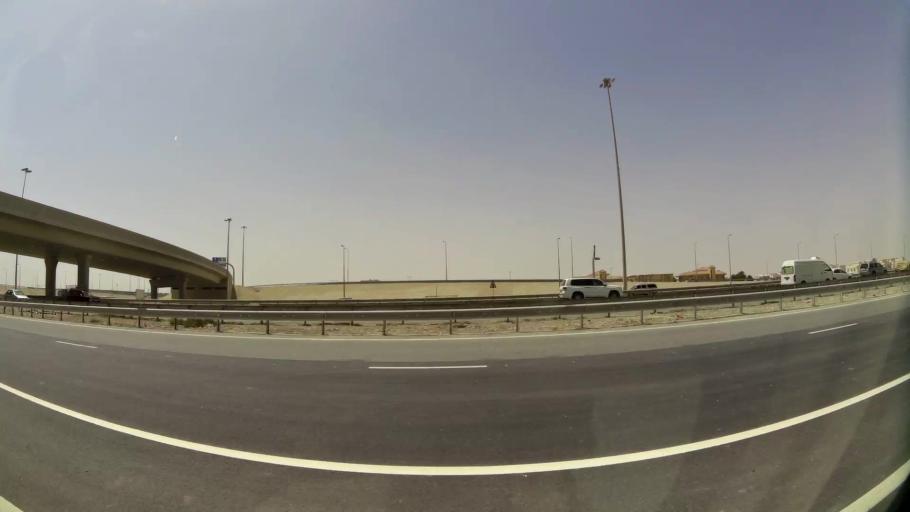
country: QA
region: Baladiyat Umm Salal
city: Umm Salal Muhammad
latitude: 25.3819
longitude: 51.4396
